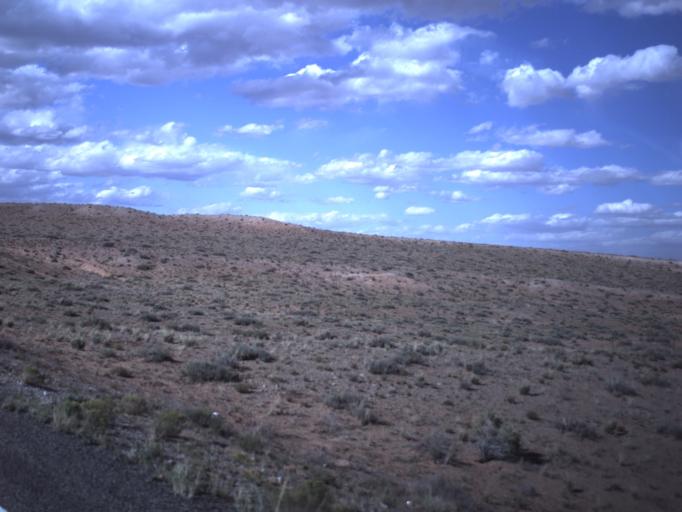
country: US
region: Utah
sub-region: Emery County
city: Ferron
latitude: 38.3318
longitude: -110.6811
